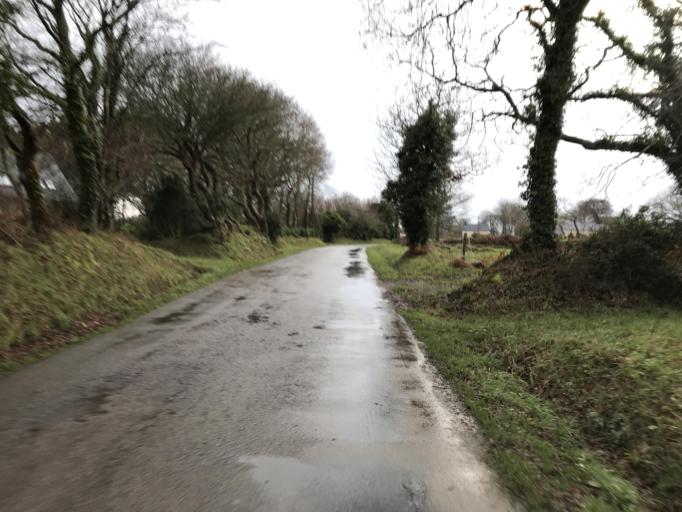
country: FR
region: Brittany
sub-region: Departement du Finistere
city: Loperhet
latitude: 48.3629
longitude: -4.3267
